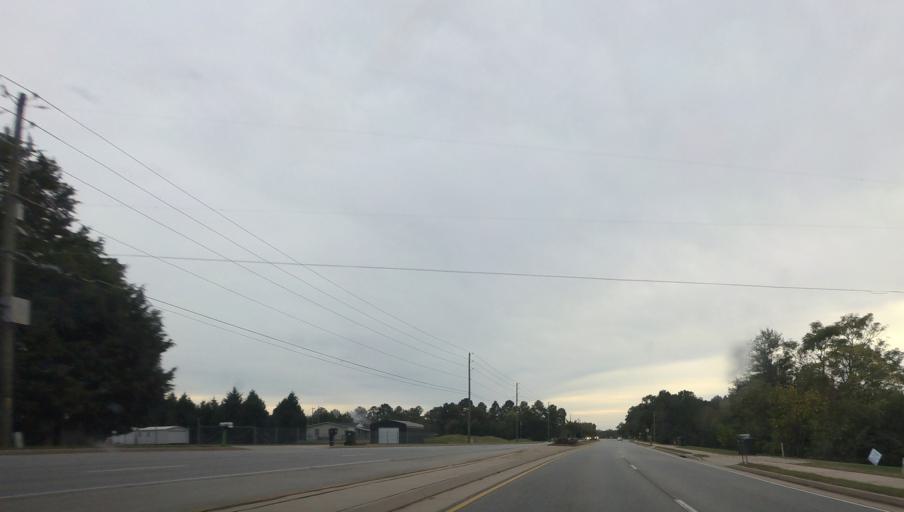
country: US
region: Georgia
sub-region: Houston County
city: Centerville
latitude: 32.5376
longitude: -83.6600
